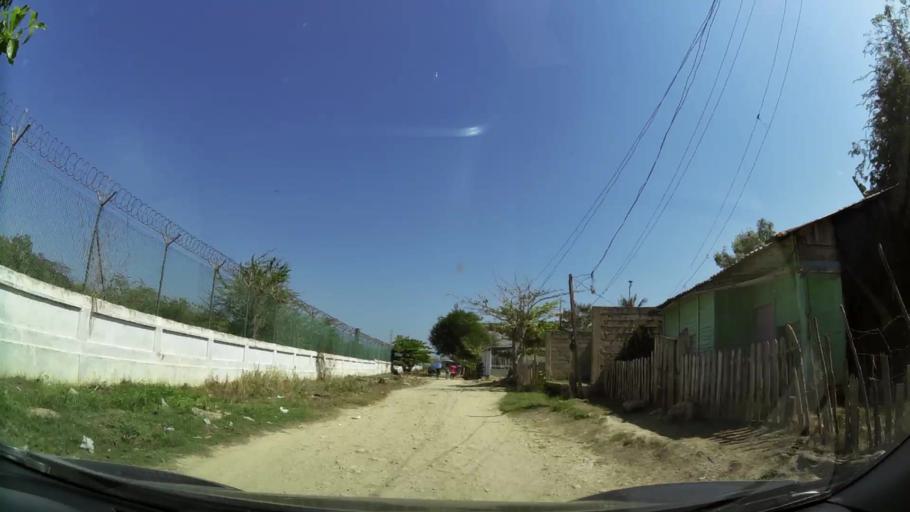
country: CO
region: Bolivar
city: Cartagena
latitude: 10.3548
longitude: -75.4872
